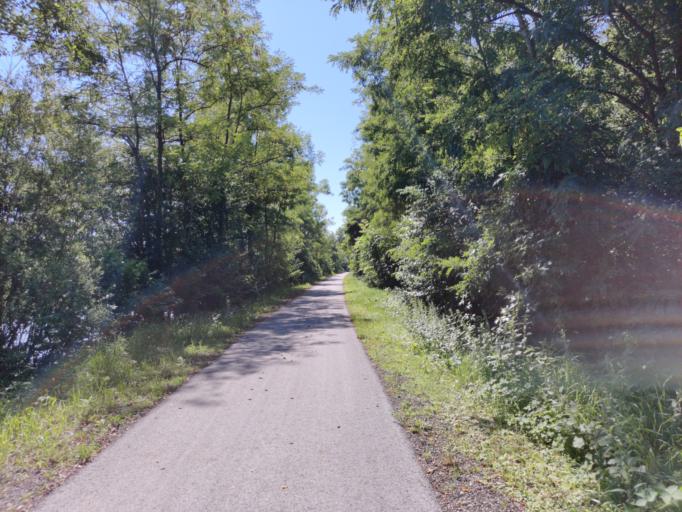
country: AT
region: Styria
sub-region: Politischer Bezirk Leibnitz
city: Stocking
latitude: 46.8596
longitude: 15.5353
